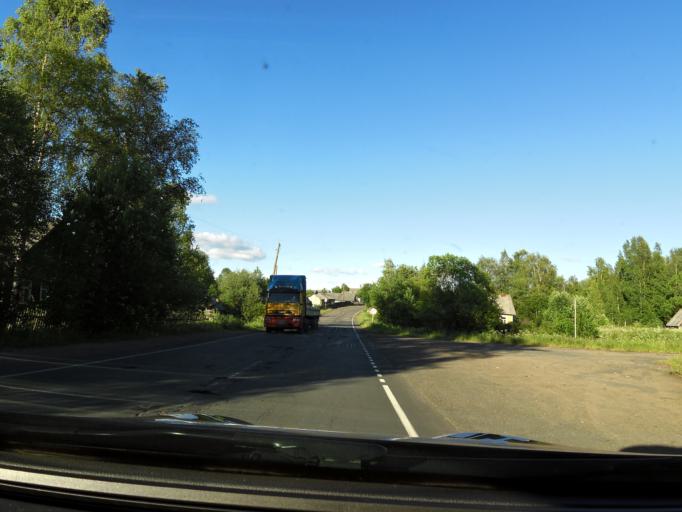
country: RU
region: Republic of Karelia
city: Kvartsitnyy
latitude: 61.4573
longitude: 35.0351
